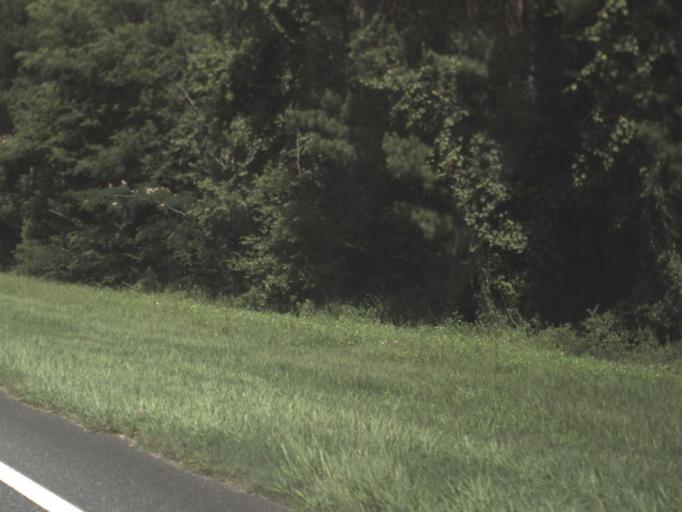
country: US
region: Florida
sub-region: Alachua County
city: Archer
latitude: 29.5413
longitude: -82.5121
